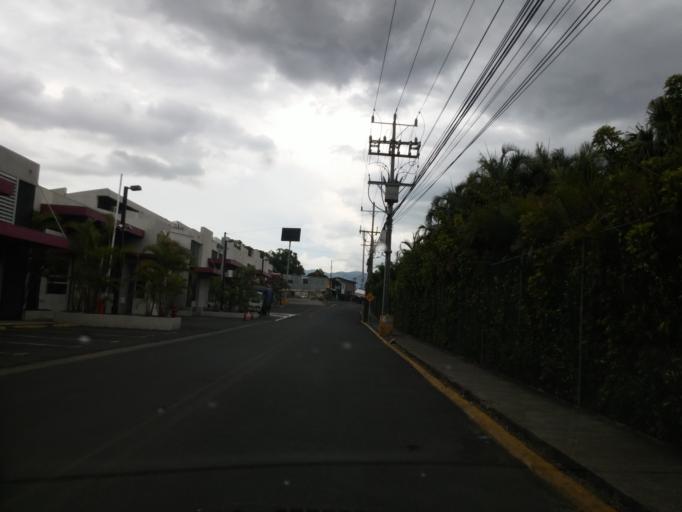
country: CR
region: Alajuela
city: Alajuela
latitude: 10.0025
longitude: -84.1949
